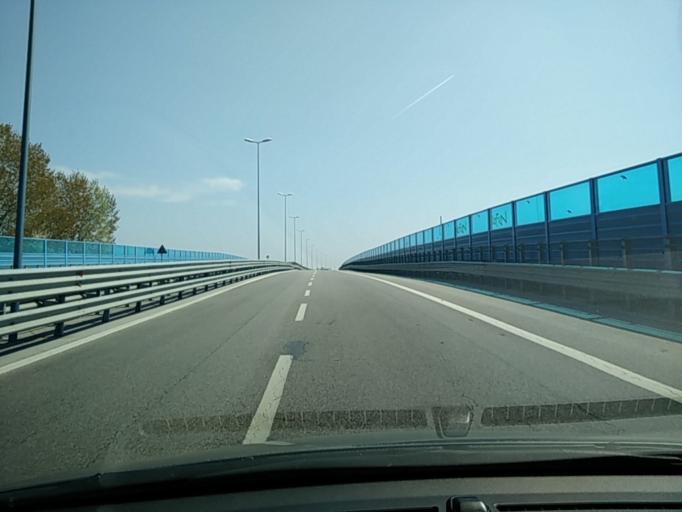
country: IT
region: Veneto
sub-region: Provincia di Treviso
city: Treviso
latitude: 45.6572
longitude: 12.2071
